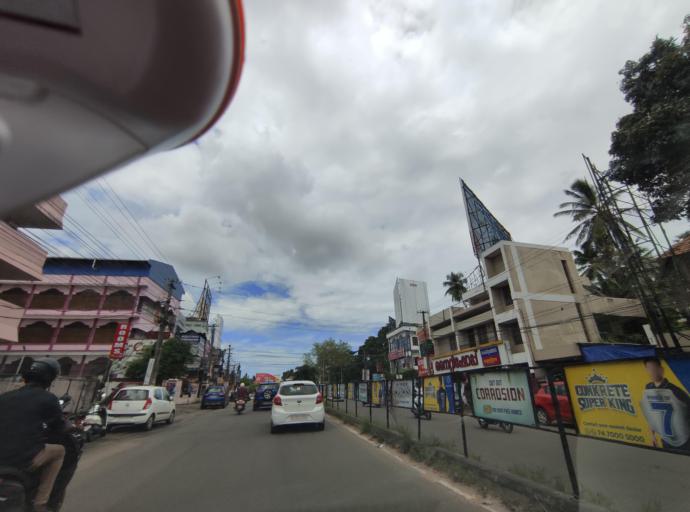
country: IN
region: Kerala
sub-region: Thiruvananthapuram
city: Thiruvananthapuram
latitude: 8.5304
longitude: 76.9389
